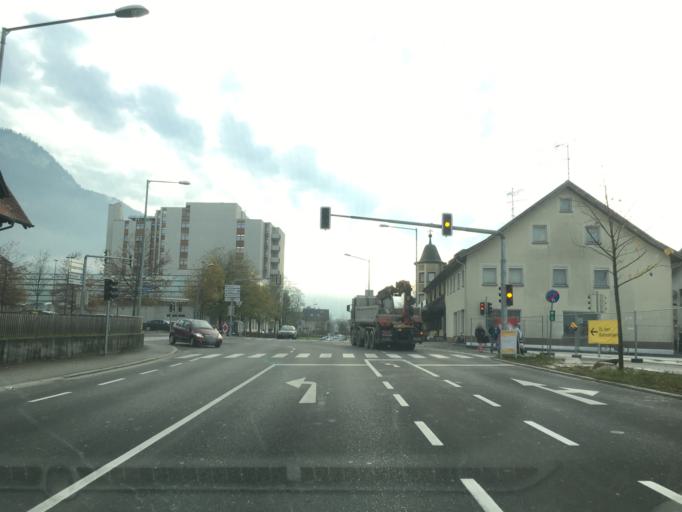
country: AT
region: Vorarlberg
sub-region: Politischer Bezirk Dornbirn
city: Hohenems
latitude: 47.3644
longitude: 9.6815
